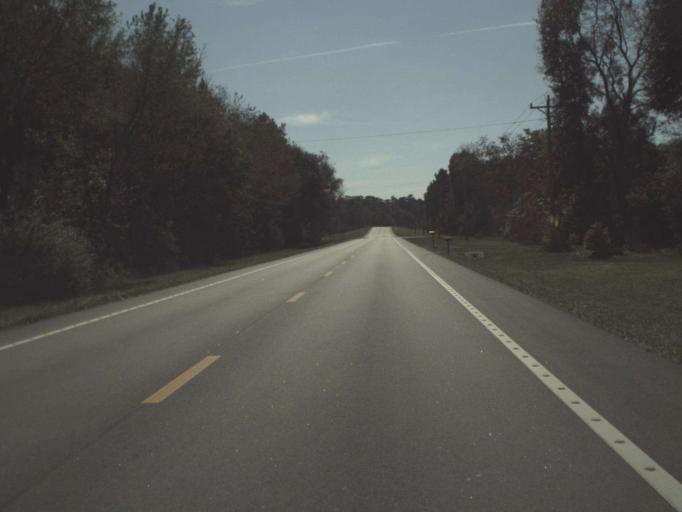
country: US
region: Florida
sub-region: Gadsden County
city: Gretna
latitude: 30.5756
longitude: -84.6730
